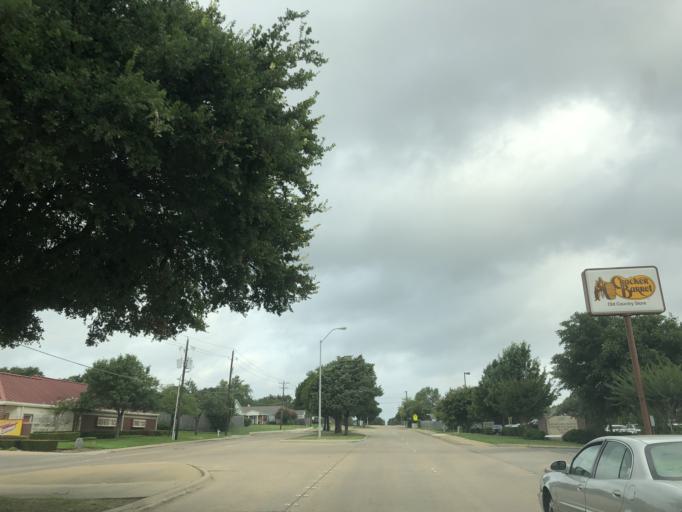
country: US
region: Texas
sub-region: Dallas County
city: Mesquite
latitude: 32.8345
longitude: -96.6346
